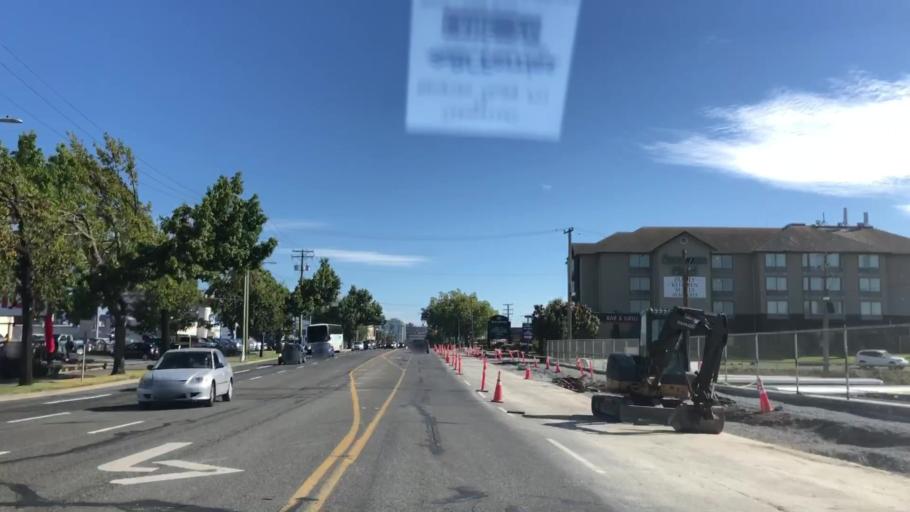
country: CA
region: British Columbia
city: Victoria
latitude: 48.4407
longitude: -123.3683
